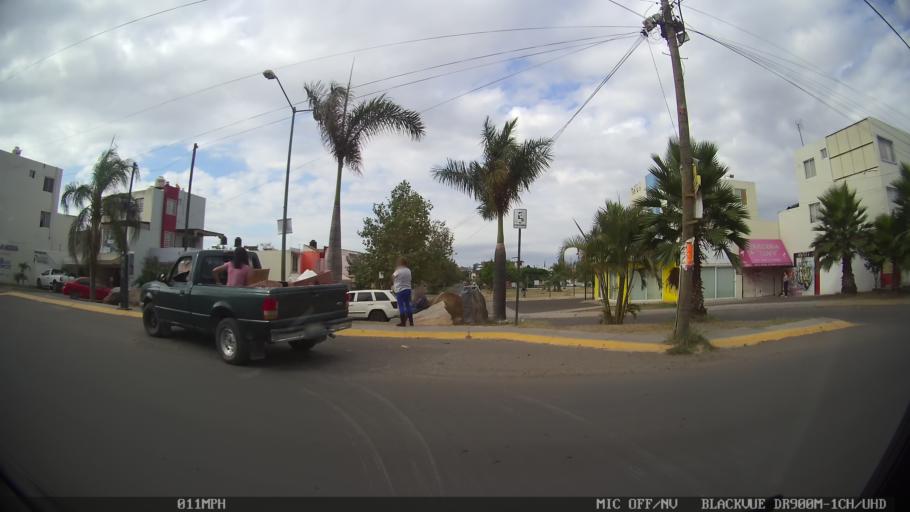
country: MX
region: Jalisco
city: Tonala
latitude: 20.6623
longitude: -103.2374
